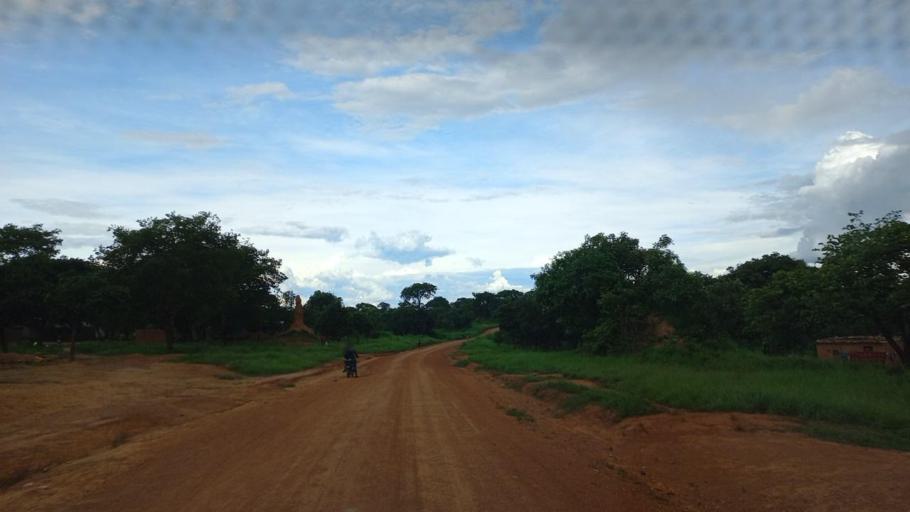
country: ZM
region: North-Western
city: Mwinilunga
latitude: -11.7594
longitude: 24.4199
